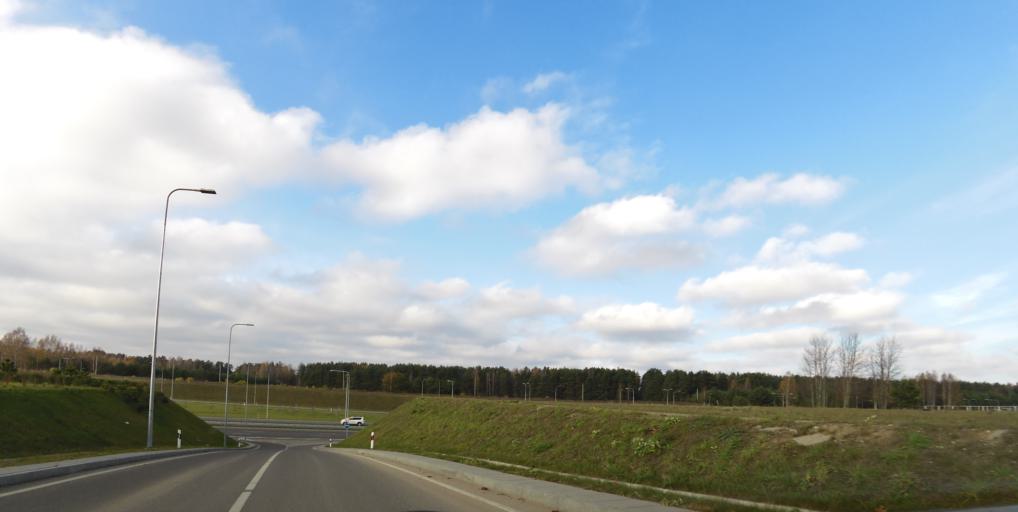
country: LT
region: Vilnius County
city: Lazdynai
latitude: 54.6844
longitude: 25.1967
